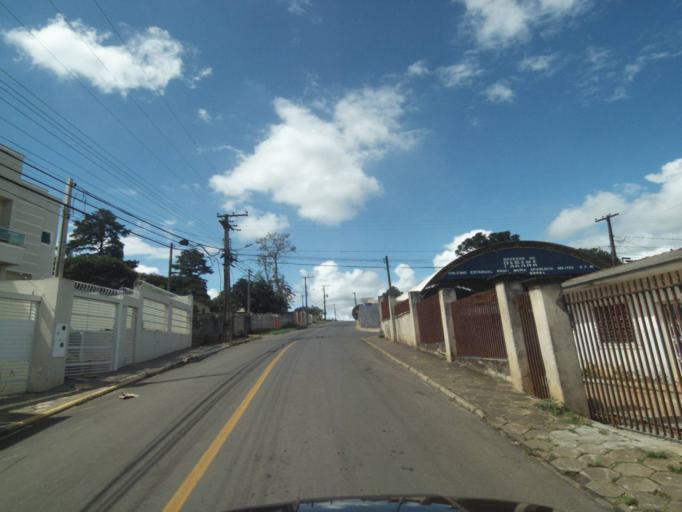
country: BR
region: Parana
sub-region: Telemaco Borba
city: Telemaco Borba
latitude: -24.3177
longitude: -50.6302
